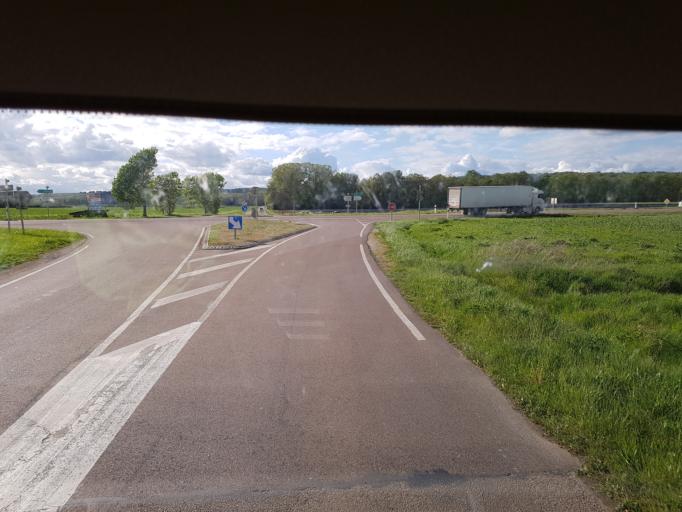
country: FR
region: Bourgogne
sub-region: Departement de l'Yonne
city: Ligny-le-Chatel
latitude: 47.9198
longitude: 3.7139
